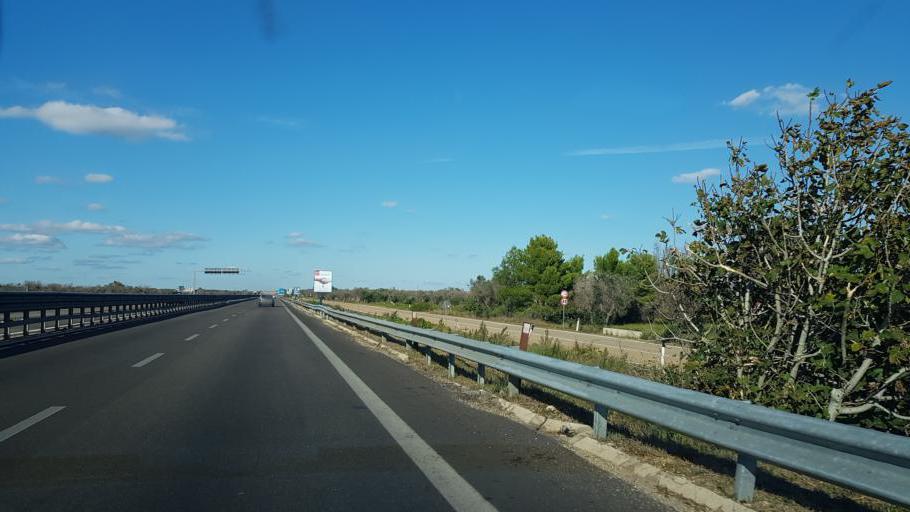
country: IT
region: Apulia
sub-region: Provincia di Lecce
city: San Pietro in Lama
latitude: 40.2588
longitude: 18.1192
